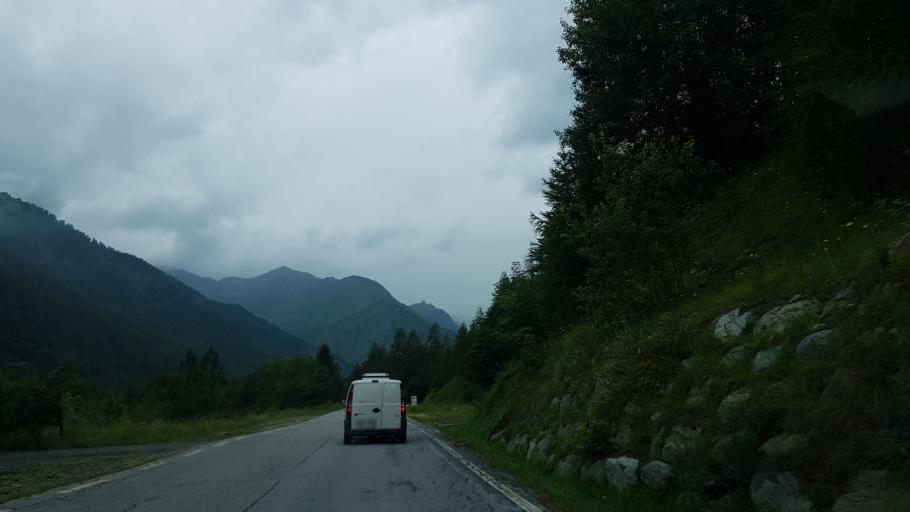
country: IT
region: Piedmont
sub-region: Provincia di Cuneo
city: Casteldelfino
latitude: 44.6094
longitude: 7.0592
